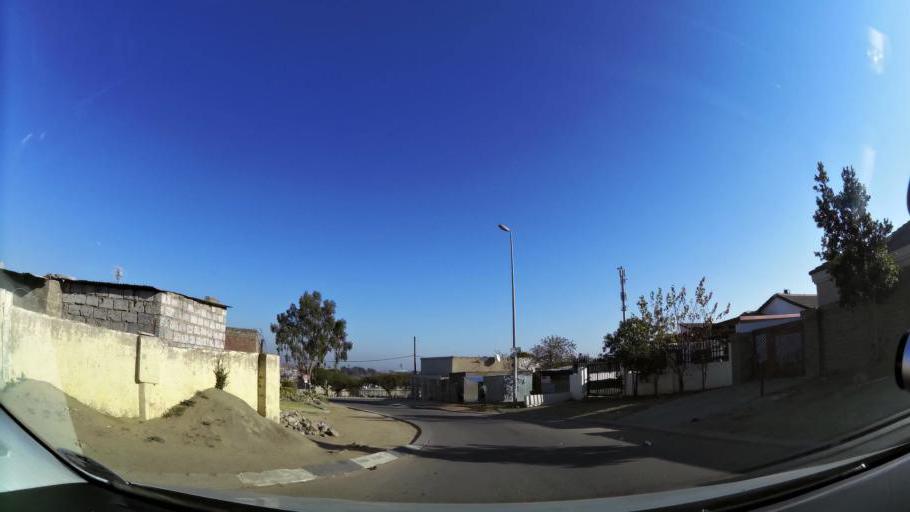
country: ZA
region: Gauteng
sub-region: City of Johannesburg Metropolitan Municipality
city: Modderfontein
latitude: -26.0450
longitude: 28.1601
